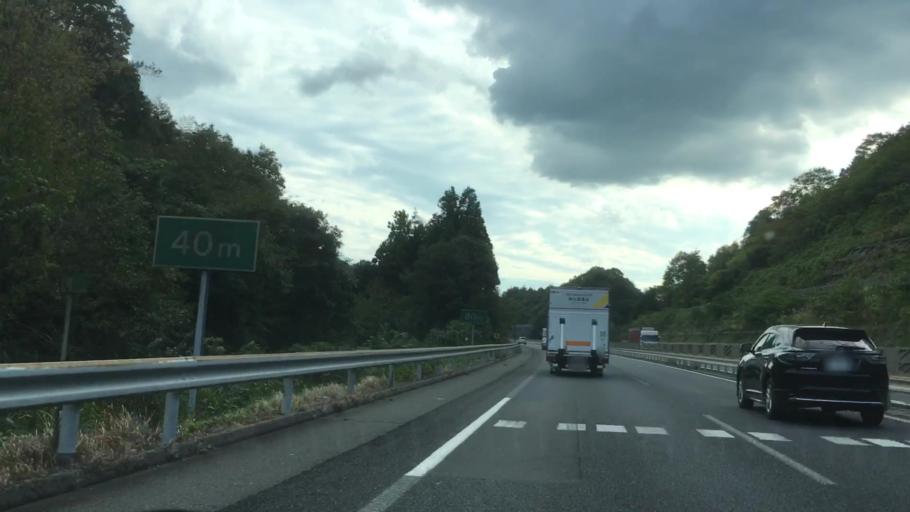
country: JP
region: Yamaguchi
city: Iwakuni
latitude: 34.1301
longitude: 132.1122
